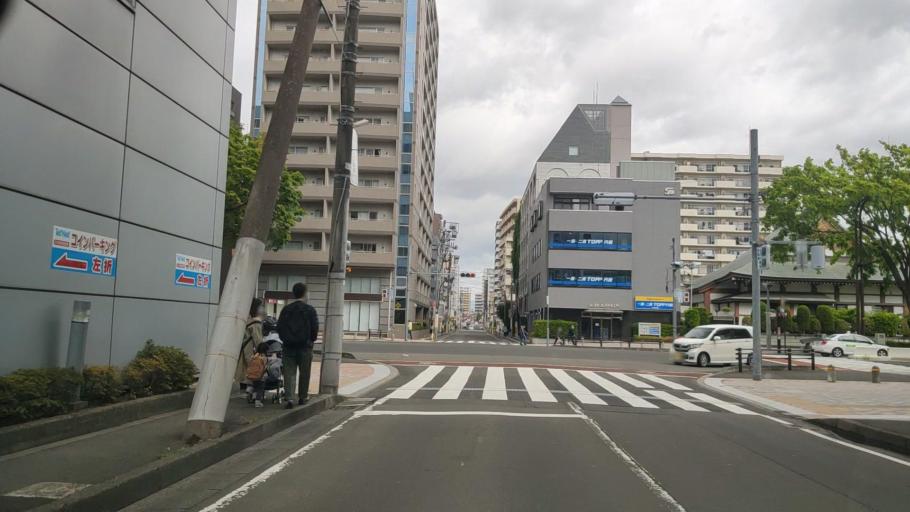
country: JP
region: Miyagi
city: Sendai-shi
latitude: 38.2590
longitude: 140.8891
